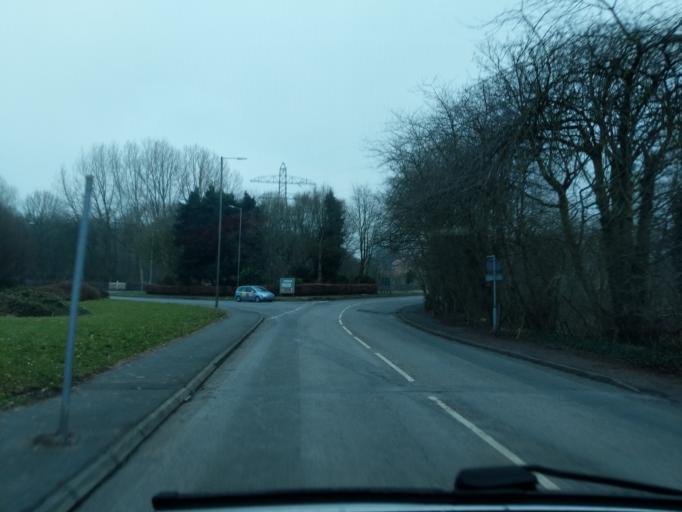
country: GB
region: England
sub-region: St. Helens
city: St Helens
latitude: 53.4707
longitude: -2.7411
